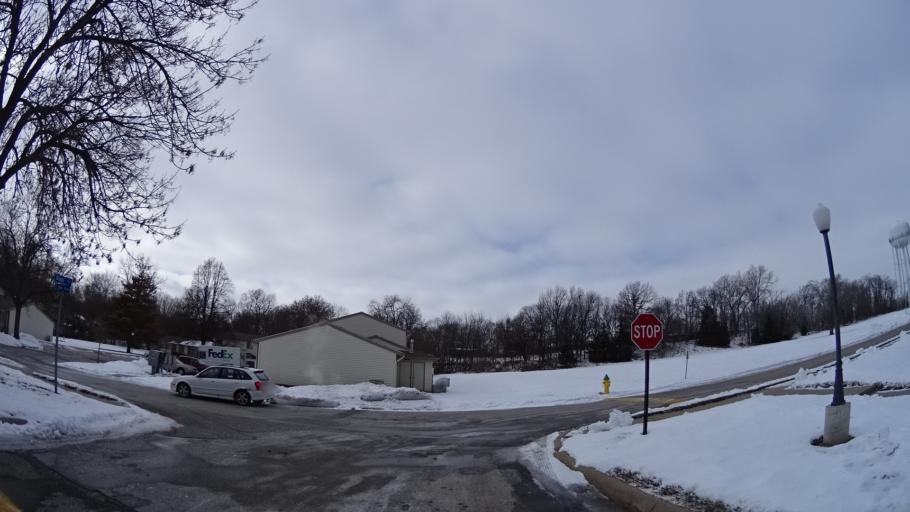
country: US
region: Nebraska
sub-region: Sarpy County
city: Offutt Air Force Base
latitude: 41.1192
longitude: -95.9556
